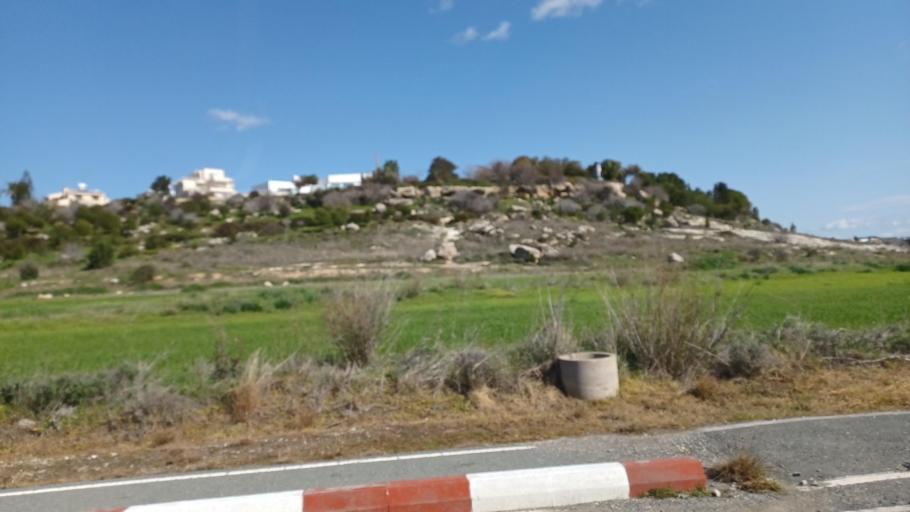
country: CY
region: Pafos
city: Paphos
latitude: 34.7551
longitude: 32.4441
